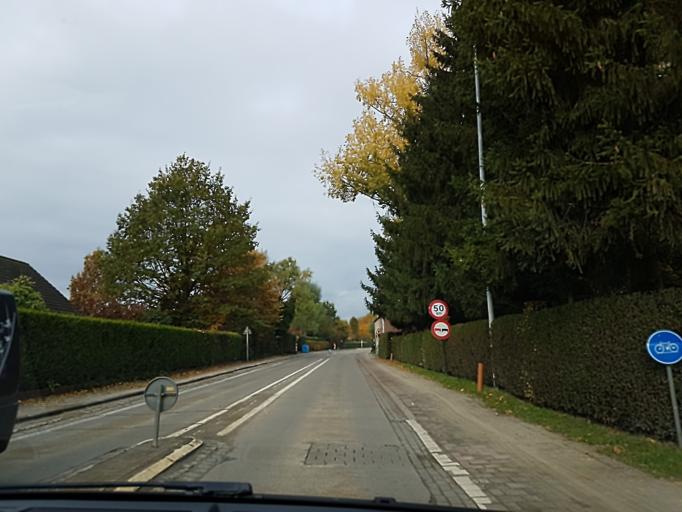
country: BE
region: Flanders
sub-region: Provincie Antwerpen
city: Boechout
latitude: 51.1461
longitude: 4.4854
